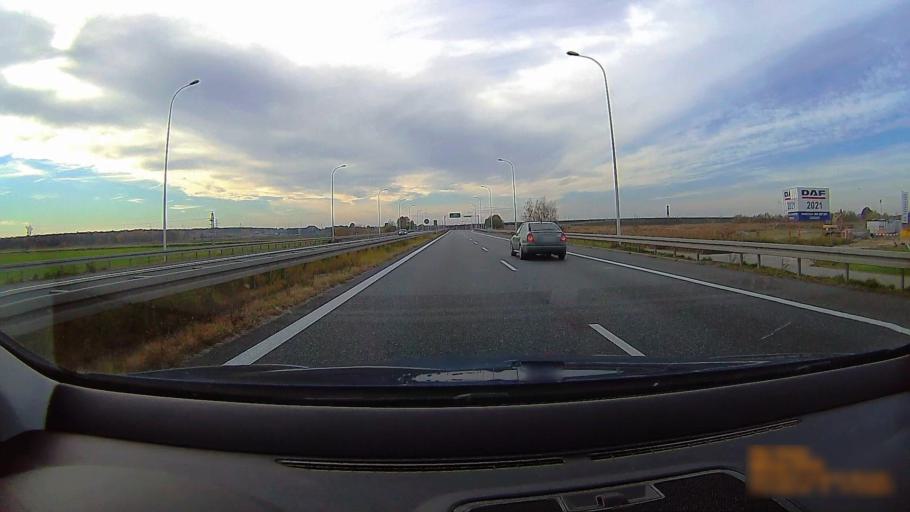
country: PL
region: Greater Poland Voivodeship
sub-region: Powiat ostrowski
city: Ostrow Wielkopolski
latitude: 51.6690
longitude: 17.8627
